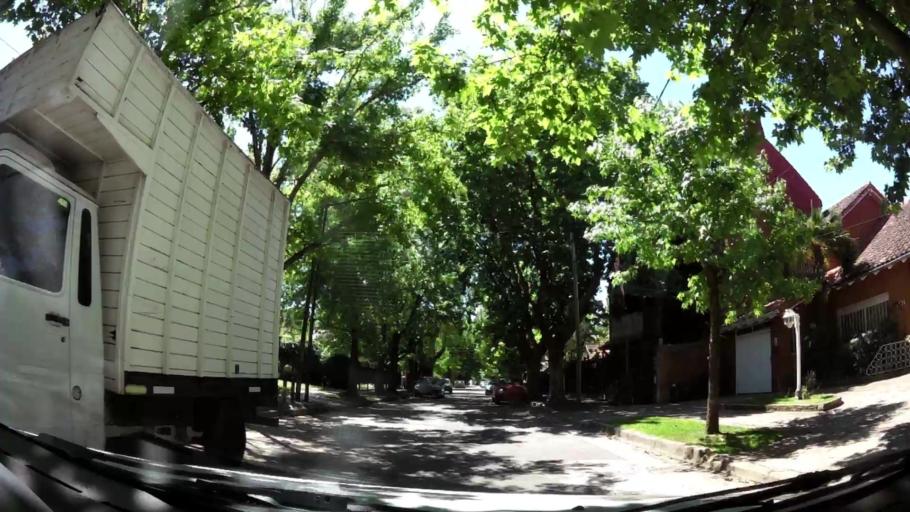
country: AR
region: Buenos Aires
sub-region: Partido de San Isidro
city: San Isidro
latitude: -34.4773
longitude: -58.4946
